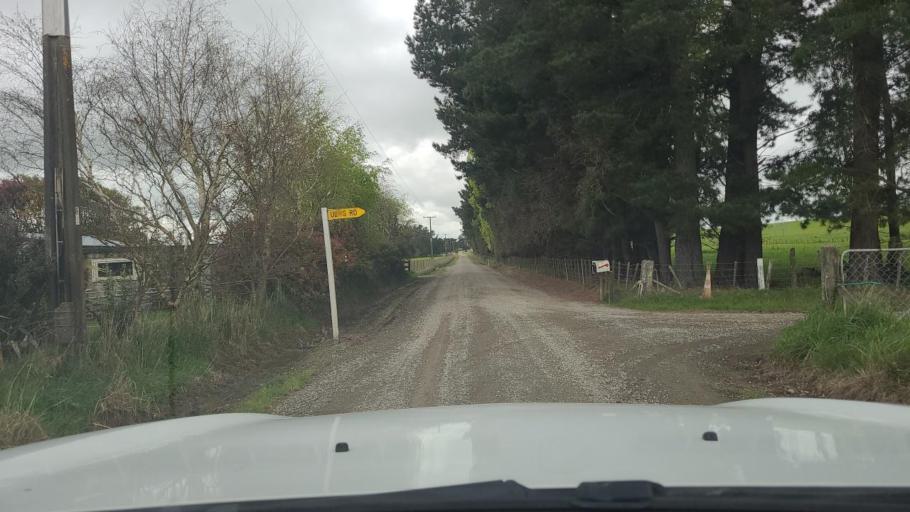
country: NZ
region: Wellington
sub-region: Masterton District
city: Masterton
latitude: -41.0539
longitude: 175.5180
